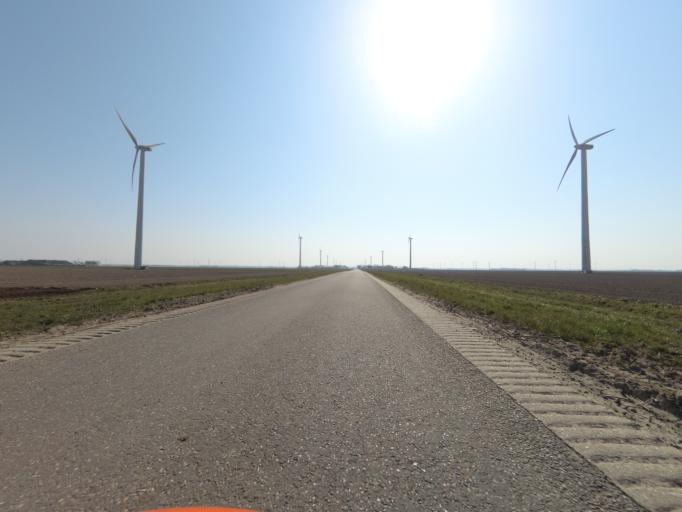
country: NL
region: Utrecht
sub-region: Gemeente Bunschoten
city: Spakenburg
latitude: 52.3509
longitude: 5.3672
